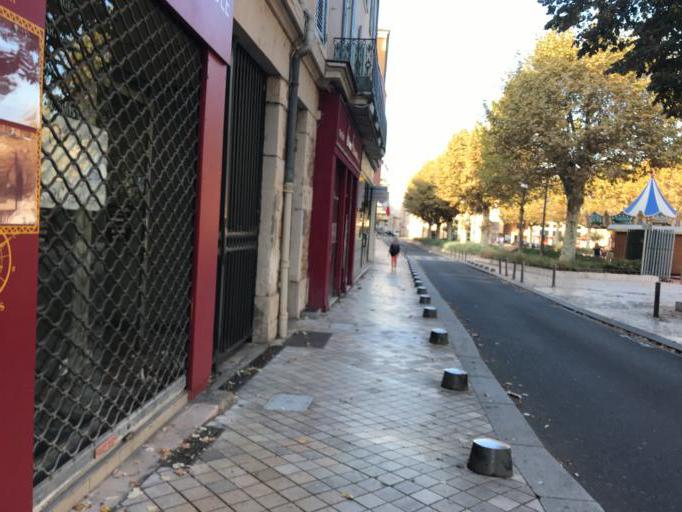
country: FR
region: Rhone-Alpes
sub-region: Departement du Rhone
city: Villefranche-sur-Saone
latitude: 45.9876
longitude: 4.7169
